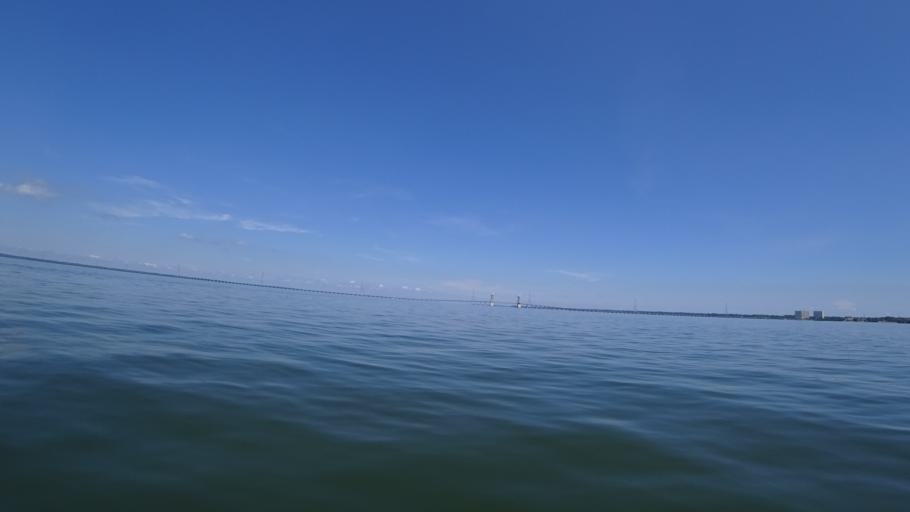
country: US
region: Virginia
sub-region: City of Newport News
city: Newport News
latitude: 36.9897
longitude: -76.4558
